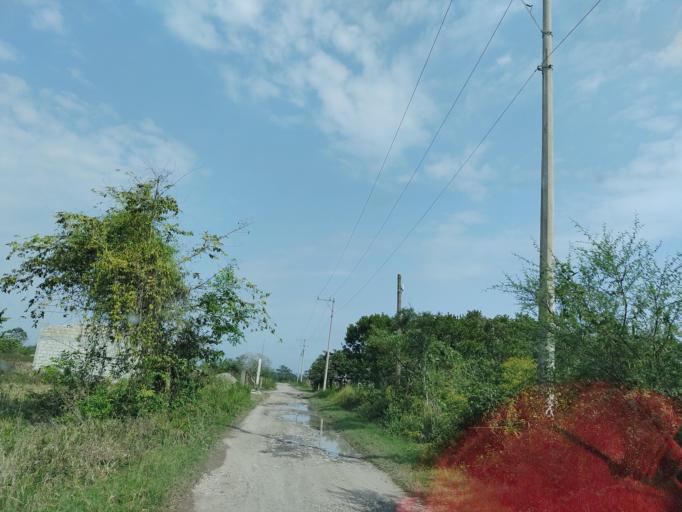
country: MX
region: Puebla
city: Espinal
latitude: 20.2798
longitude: -97.3328
